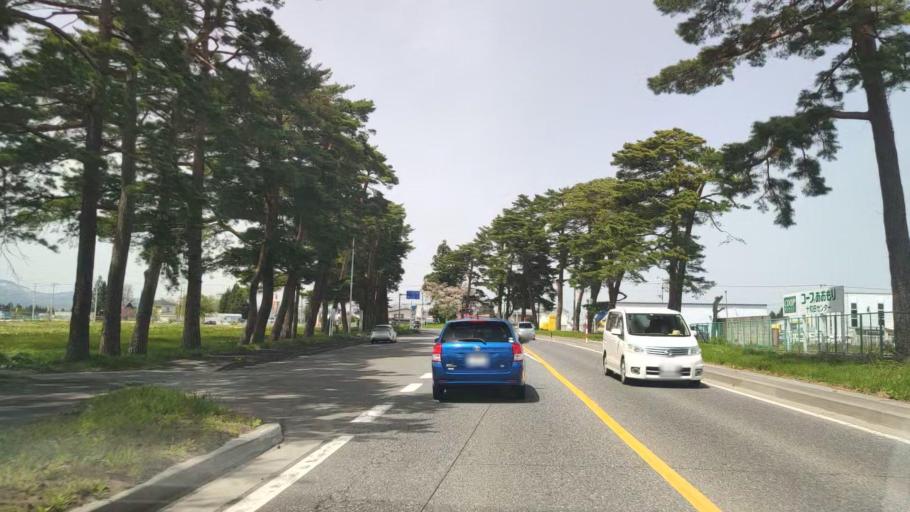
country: JP
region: Aomori
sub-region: Misawa Shi
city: Inuotose
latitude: 40.6717
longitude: 141.1827
